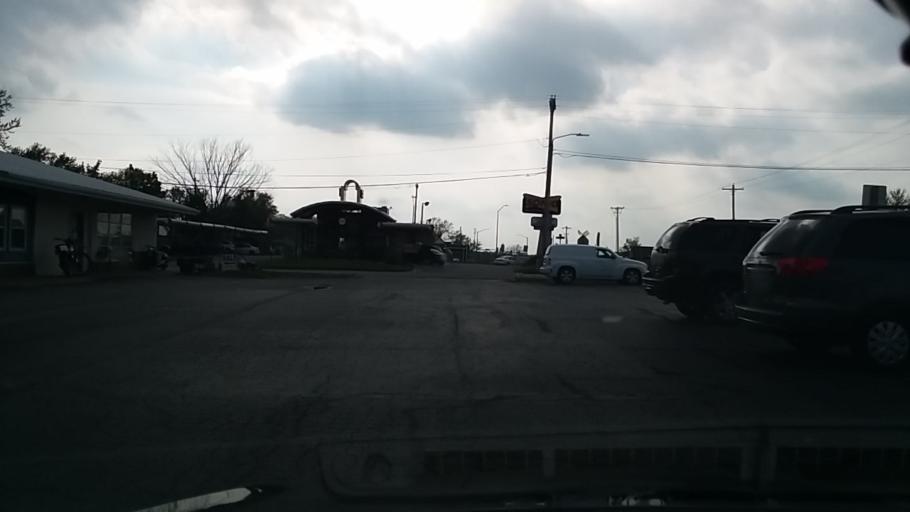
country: US
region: Kansas
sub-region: Douglas County
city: Baldwin City
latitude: 38.7820
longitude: -95.1834
